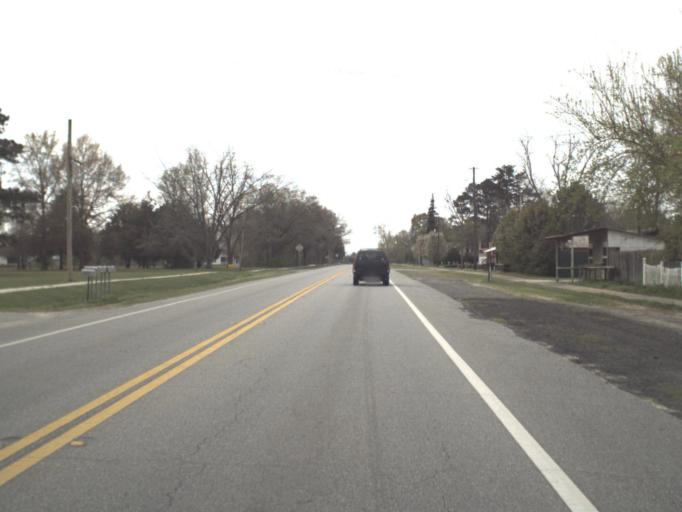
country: US
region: Alabama
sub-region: Geneva County
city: Hartford
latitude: 30.9848
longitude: -85.6464
